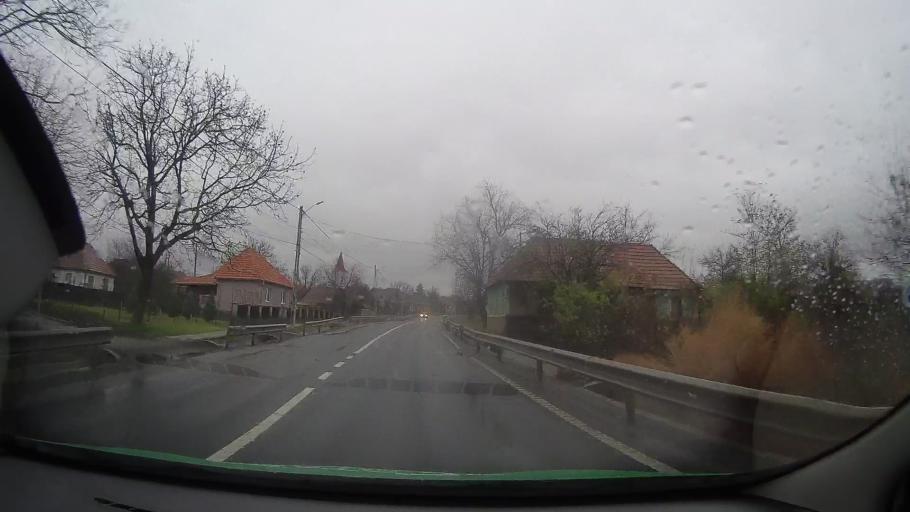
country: RO
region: Mures
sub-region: Comuna Brancovenesti
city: Brancovenesti
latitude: 46.8520
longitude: 24.7542
